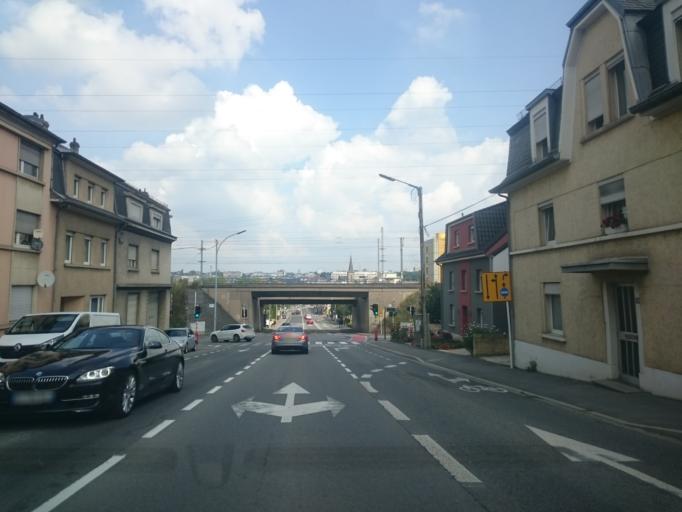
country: LU
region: Luxembourg
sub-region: Canton de Luxembourg
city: Luxembourg
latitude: 49.5953
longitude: 6.1174
